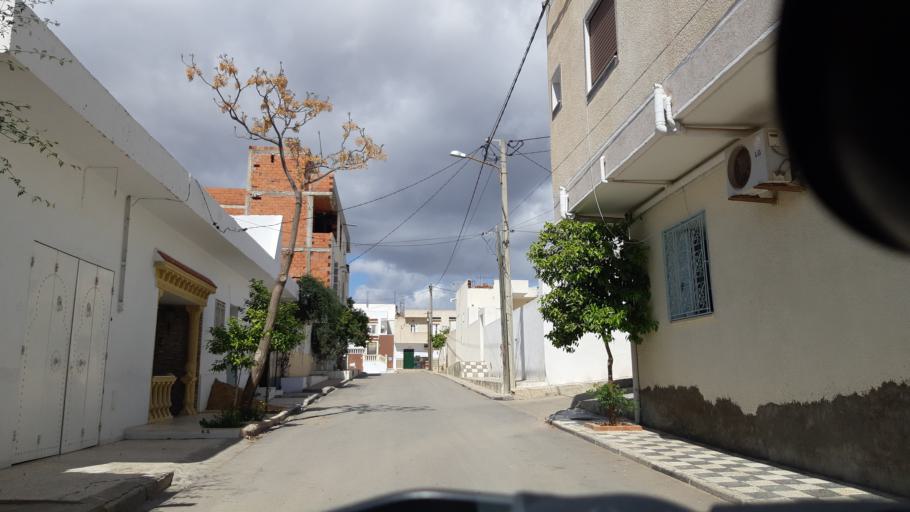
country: TN
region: Susah
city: Akouda
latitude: 35.8827
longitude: 10.5357
